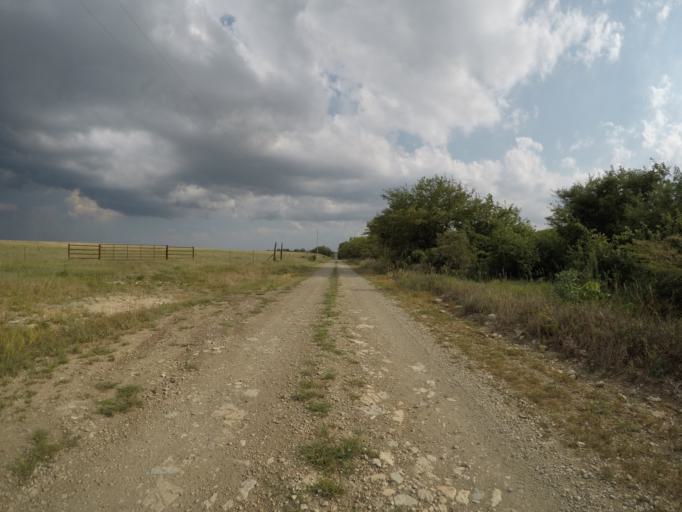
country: US
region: Kansas
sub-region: Marshall County
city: Blue Rapids
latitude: 39.5286
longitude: -96.8292
